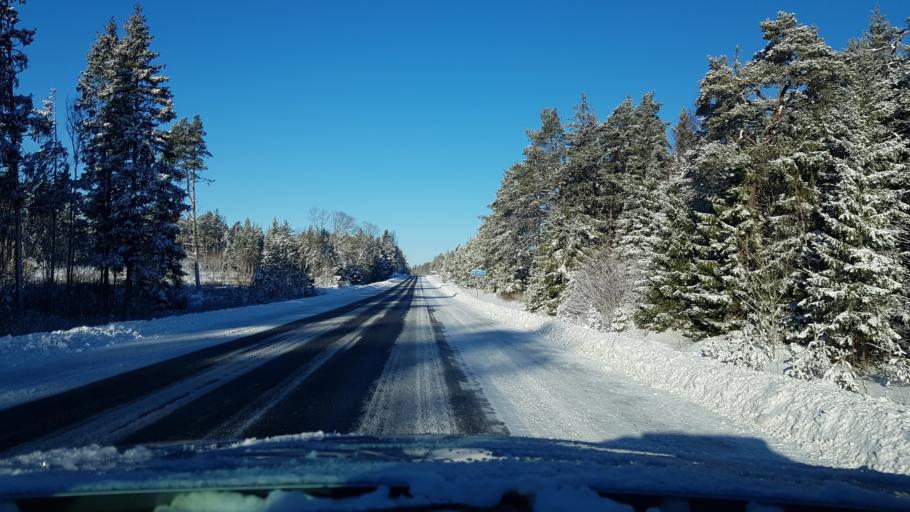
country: EE
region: Hiiumaa
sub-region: Kaerdla linn
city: Kardla
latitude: 58.9685
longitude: 22.8300
